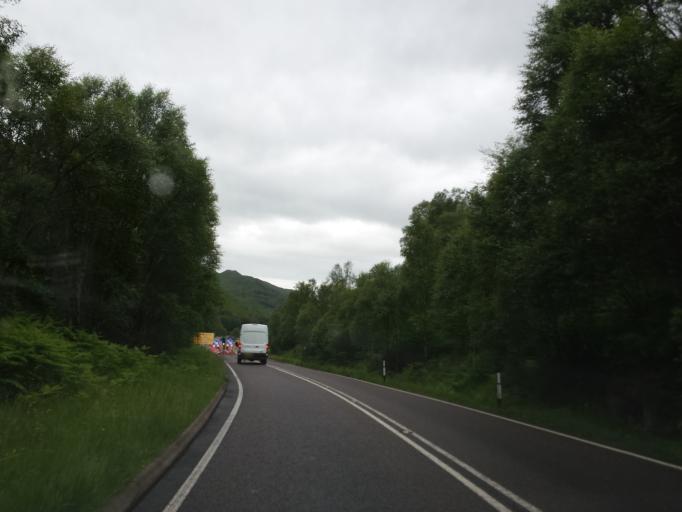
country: GB
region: Scotland
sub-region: Highland
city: Fort William
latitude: 56.8785
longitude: -5.5528
